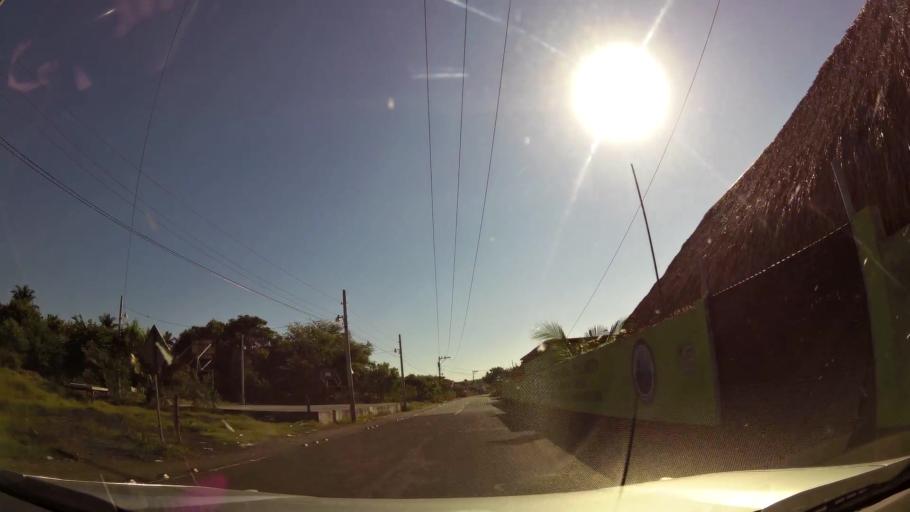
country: GT
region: Santa Rosa
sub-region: Municipio de Taxisco
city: Taxisco
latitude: 13.8849
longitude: -90.4621
